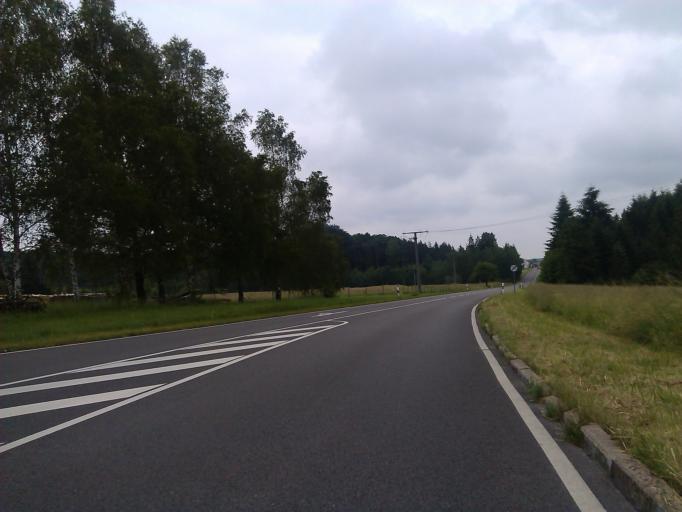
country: DE
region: Baden-Wuerttemberg
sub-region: Regierungsbezirk Stuttgart
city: Wustenrot
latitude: 49.0963
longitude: 9.4658
